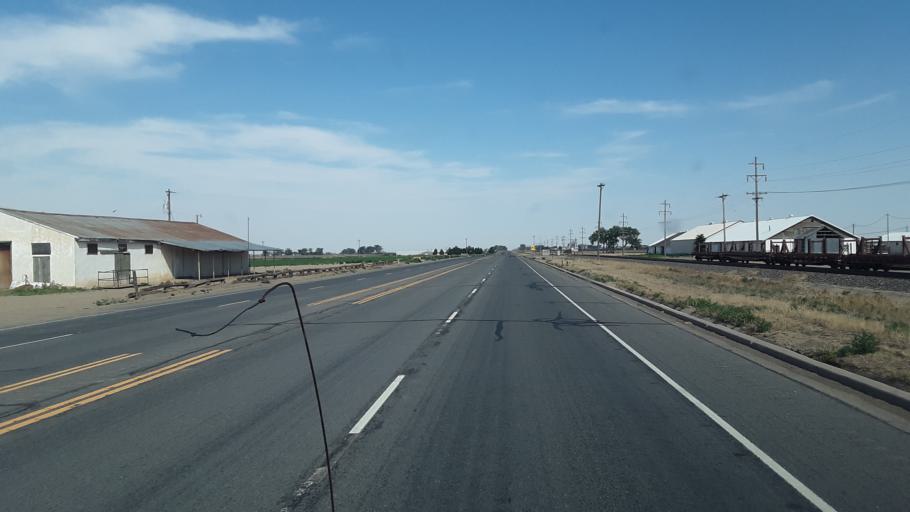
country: US
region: Colorado
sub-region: Otero County
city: Rocky Ford
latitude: 38.0880
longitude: -103.8068
